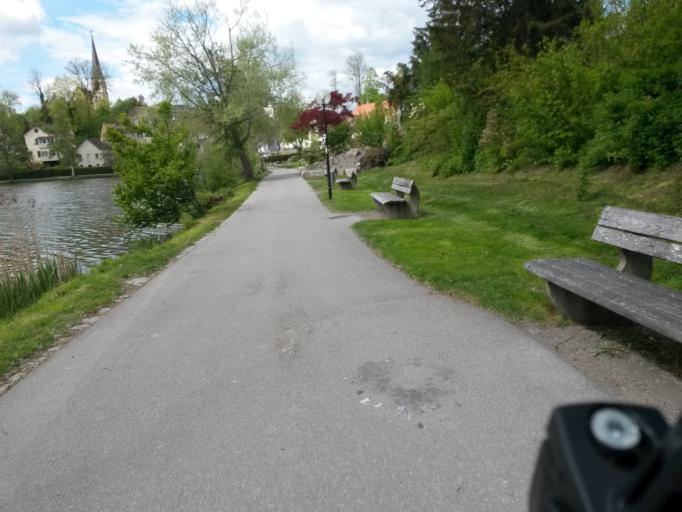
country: DE
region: Baden-Wuerttemberg
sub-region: Tuebingen Region
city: Bad Waldsee
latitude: 47.9244
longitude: 9.7540
